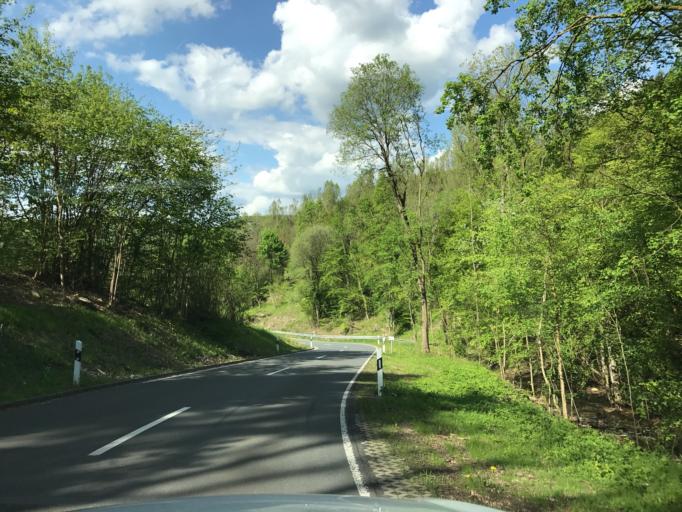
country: DE
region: Bavaria
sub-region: Upper Franconia
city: Egloffstein
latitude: 49.7237
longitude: 11.2282
